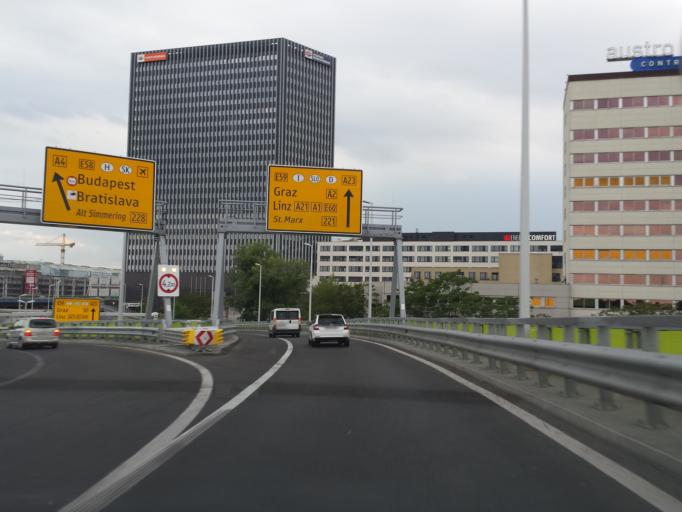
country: AT
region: Vienna
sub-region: Wien Stadt
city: Vienna
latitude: 48.1940
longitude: 16.4140
